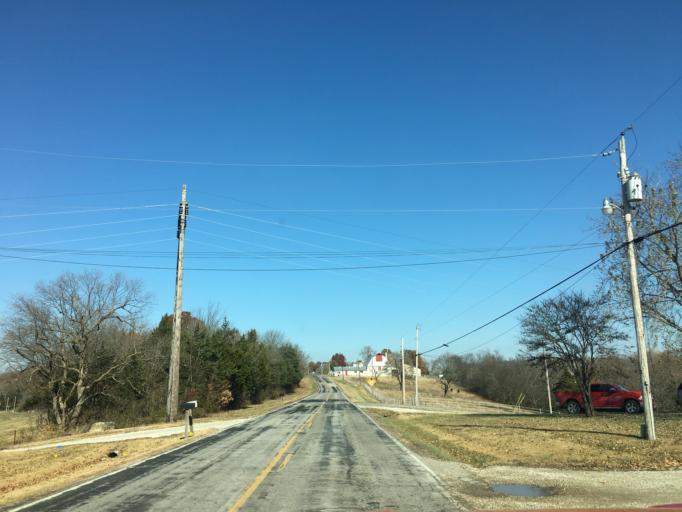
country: US
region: Missouri
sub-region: Cole County
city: Wardsville
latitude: 38.4763
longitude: -92.1776
